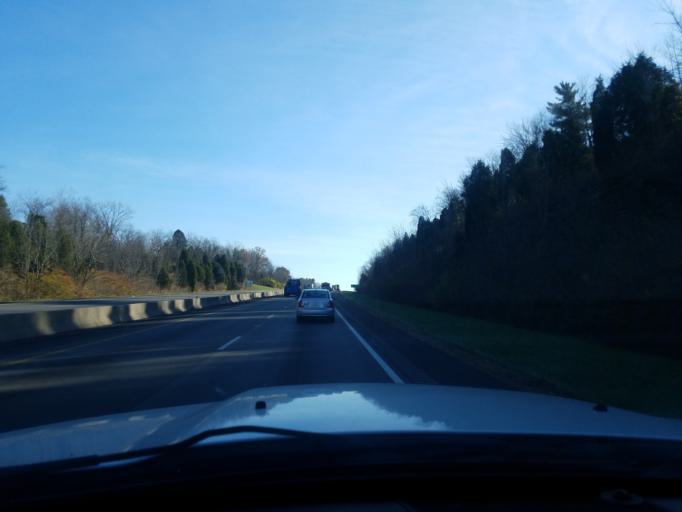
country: US
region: Ohio
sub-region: Clermont County
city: Batavia
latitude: 39.0860
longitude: -84.1627
